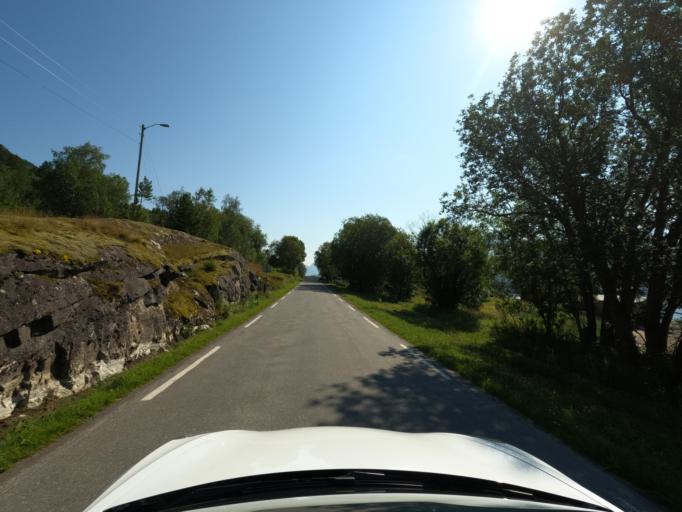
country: NO
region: Nordland
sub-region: Narvik
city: Narvik
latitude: 68.3340
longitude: 17.2779
